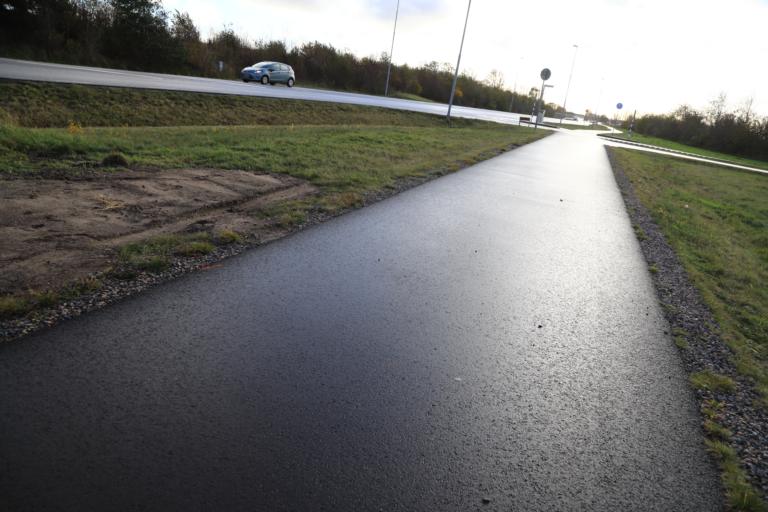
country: SE
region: Halland
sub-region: Varbergs Kommun
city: Traslovslage
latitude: 57.0863
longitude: 12.2853
